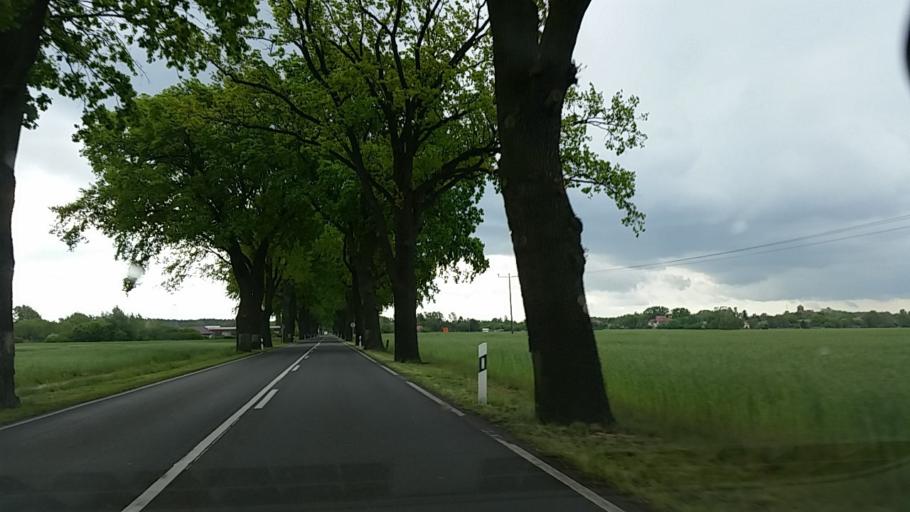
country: DE
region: Brandenburg
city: Storkow
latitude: 52.2675
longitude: 13.9279
